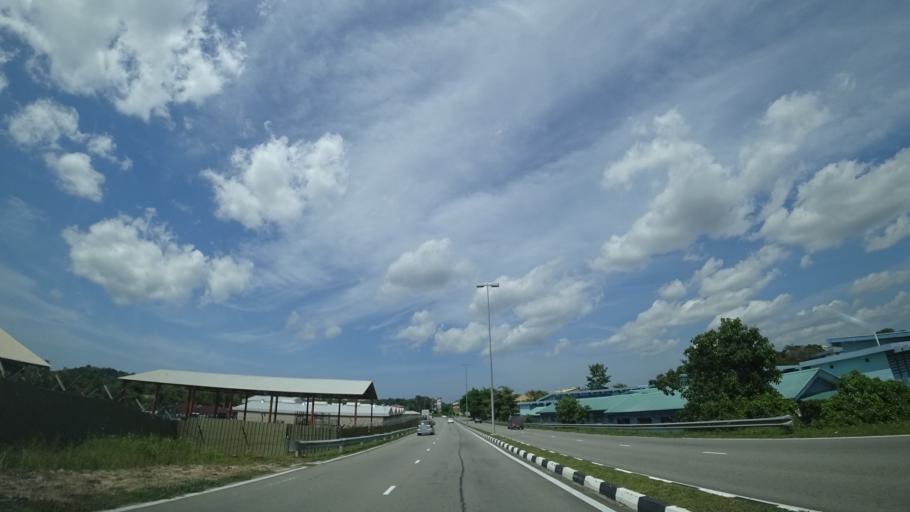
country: BN
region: Brunei and Muara
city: Bandar Seri Begawan
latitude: 4.9043
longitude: 114.9102
